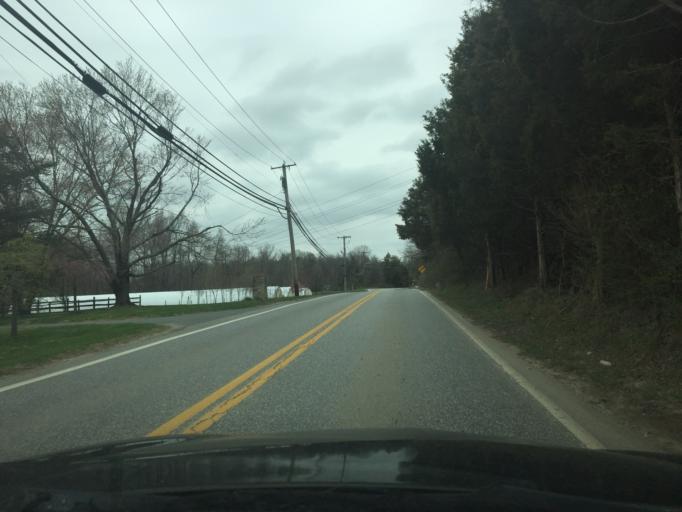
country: US
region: Maryland
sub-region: Baltimore County
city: Bowleys Quarters
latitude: 39.3533
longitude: -76.3944
